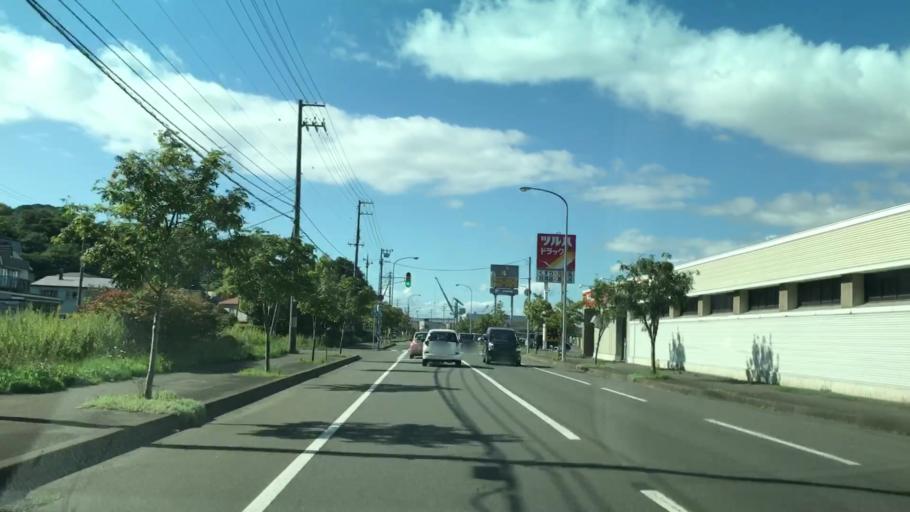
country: JP
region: Hokkaido
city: Muroran
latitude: 42.3312
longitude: 140.9650
